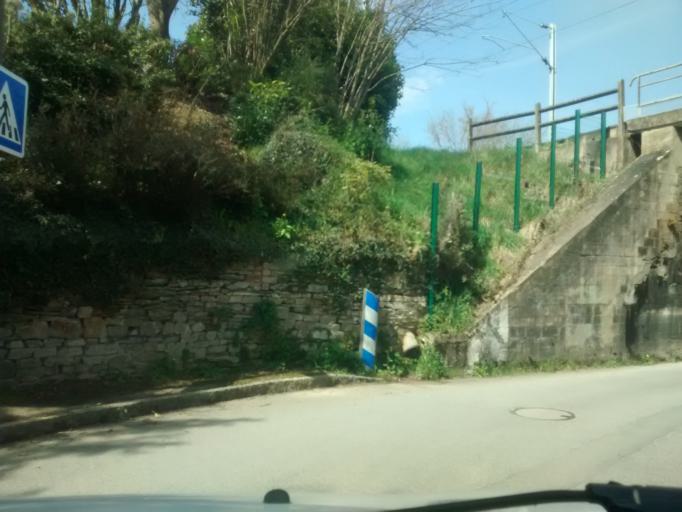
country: FR
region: Brittany
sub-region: Departement d'Ille-et-Vilaine
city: Brece
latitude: 48.1112
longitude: -1.4837
